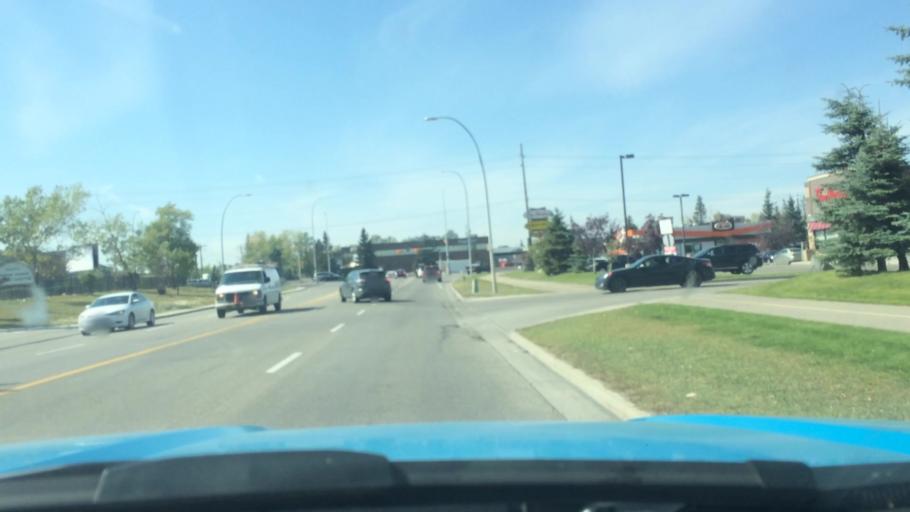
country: CA
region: Alberta
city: Calgary
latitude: 51.0888
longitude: -113.9992
